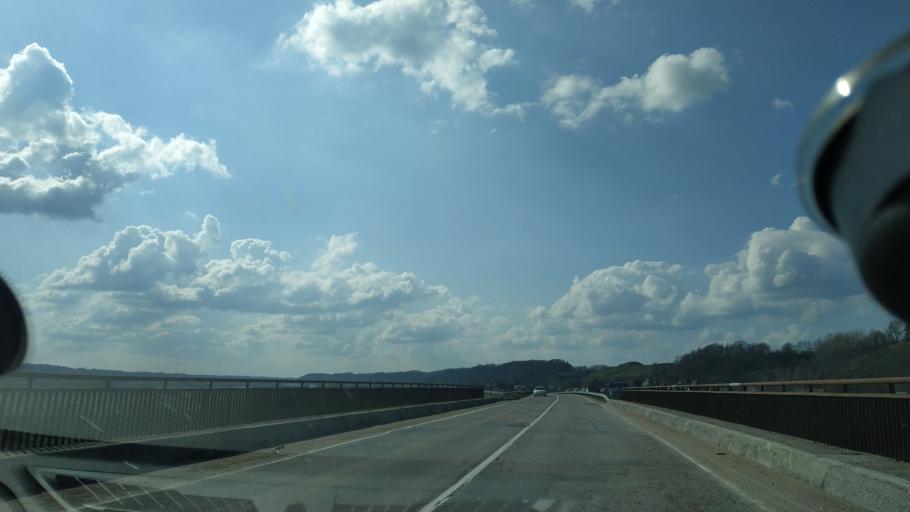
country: LT
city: Vilkija
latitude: 55.0773
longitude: 23.4202
